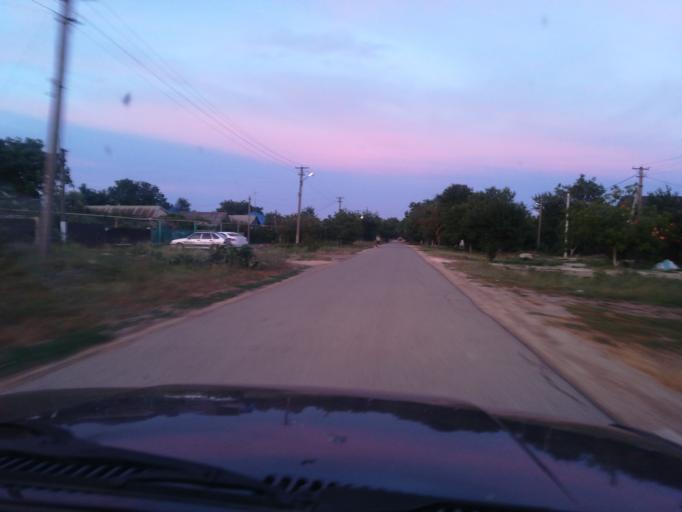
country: RU
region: Krasnodarskiy
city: Yurovka
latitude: 45.1142
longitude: 37.4301
